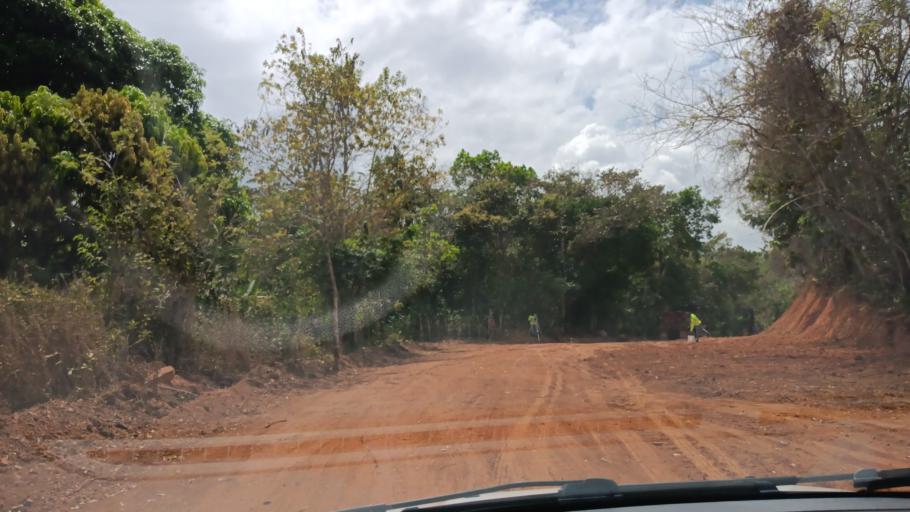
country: PA
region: Panama
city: La Cabima
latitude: 9.1205
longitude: -79.4951
